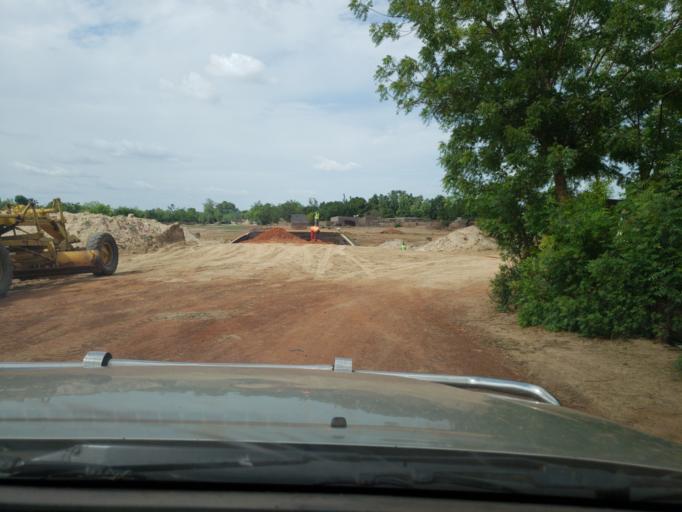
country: ML
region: Segou
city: Bla
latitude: 12.7308
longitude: -5.6711
